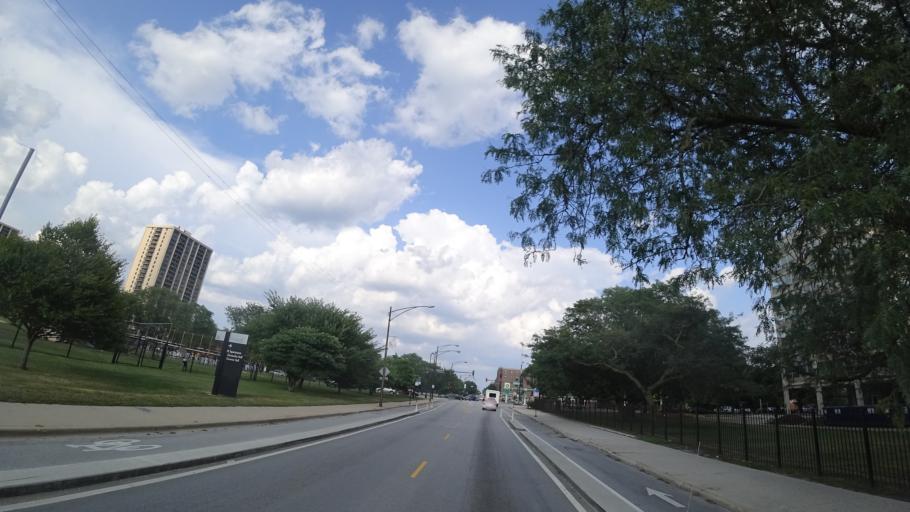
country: US
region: Illinois
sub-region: Cook County
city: Chicago
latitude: 41.8383
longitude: -87.6245
